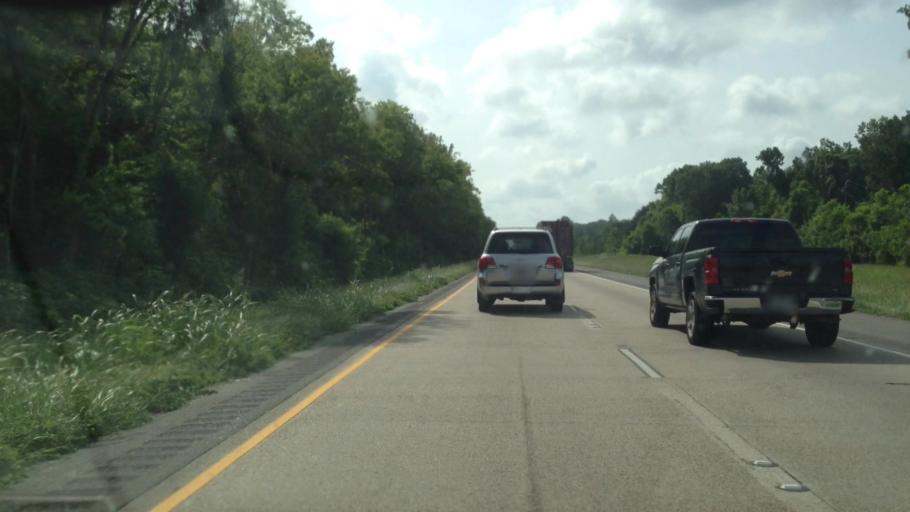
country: US
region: Louisiana
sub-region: Ascension Parish
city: Sorrento
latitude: 30.1836
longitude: -90.9026
